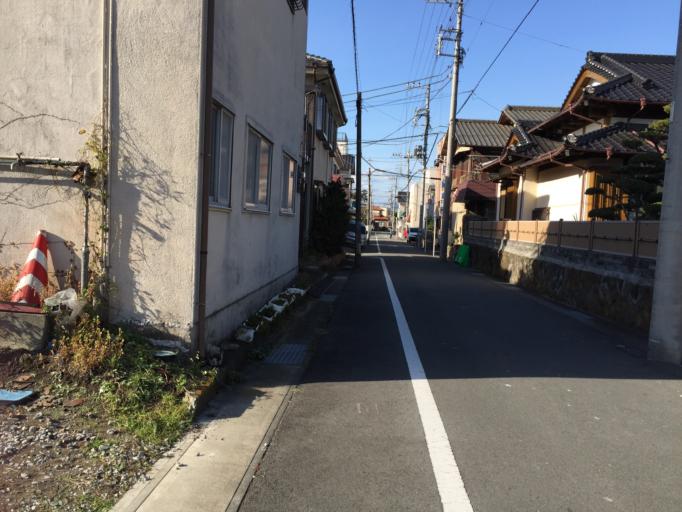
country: JP
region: Shizuoka
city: Numazu
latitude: 35.0773
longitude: 138.8601
